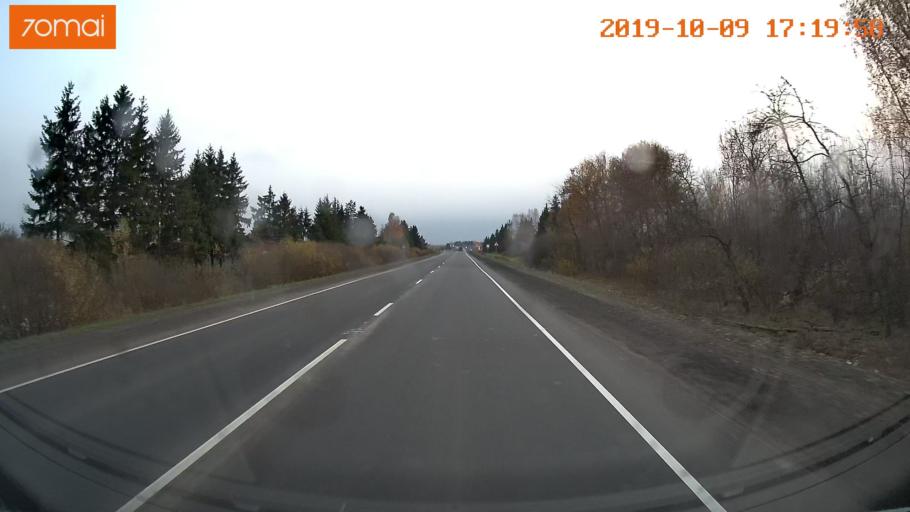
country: RU
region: Ivanovo
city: Furmanov
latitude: 57.2397
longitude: 41.1465
